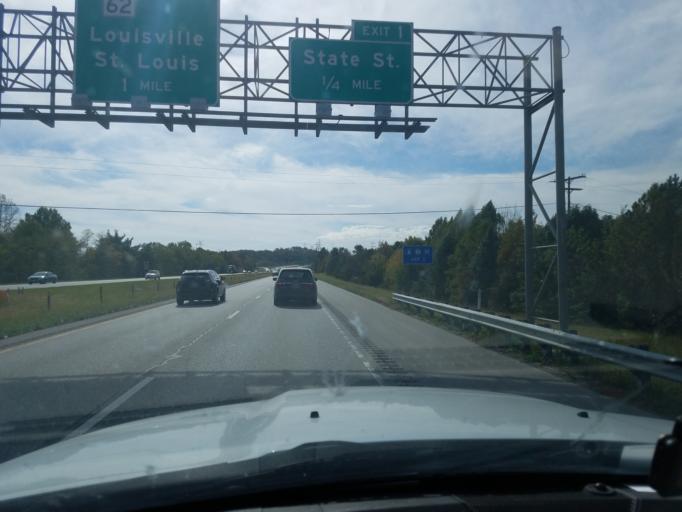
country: US
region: Indiana
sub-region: Floyd County
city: New Albany
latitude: 38.3199
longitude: -85.8407
